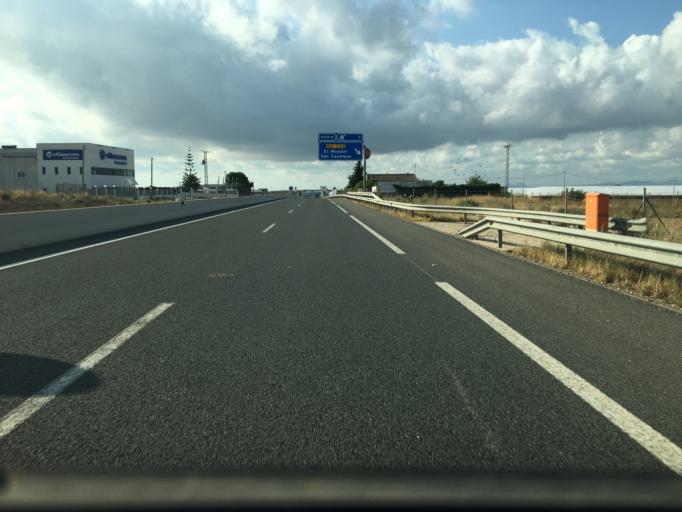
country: ES
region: Murcia
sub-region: Murcia
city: San Javier
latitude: 37.8450
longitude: -0.8730
